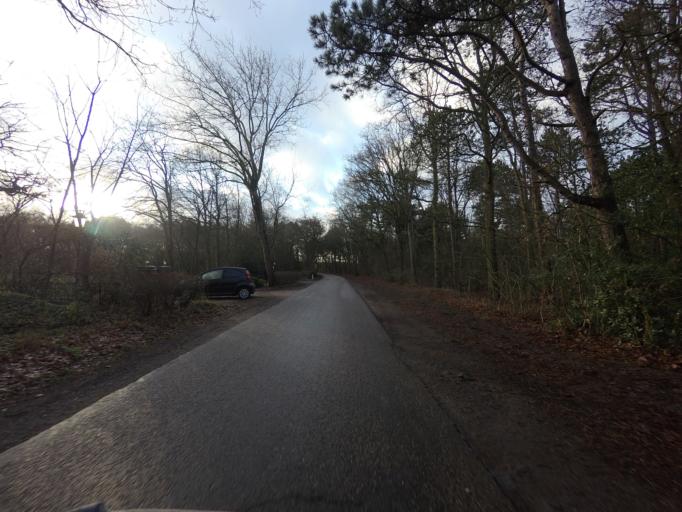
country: NL
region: North Holland
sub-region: Gemeente Texel
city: Den Burg
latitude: 53.0965
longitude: 4.7731
